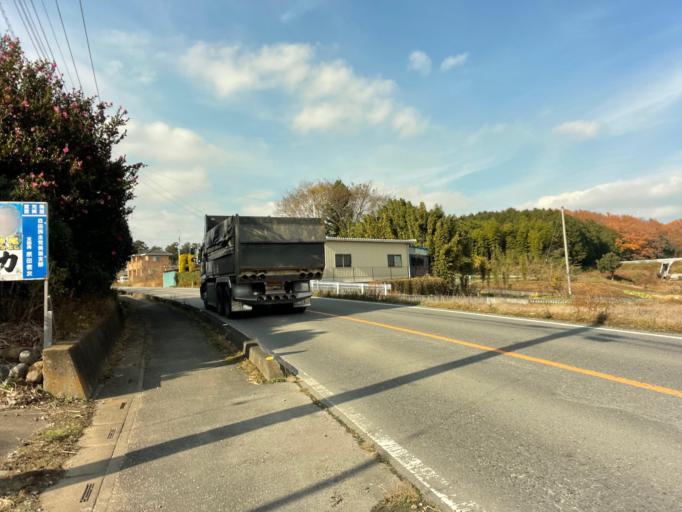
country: JP
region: Saitama
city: Yorii
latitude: 36.1566
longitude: 139.1904
